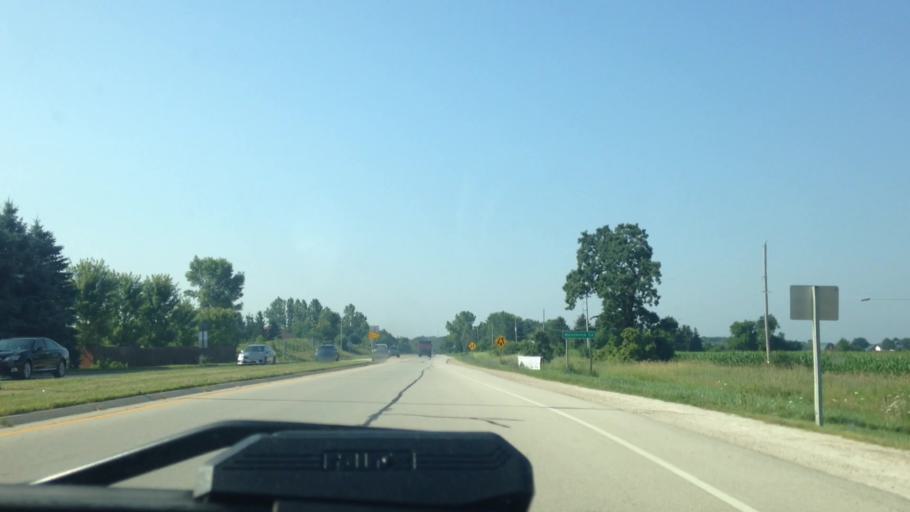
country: US
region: Wisconsin
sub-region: Waukesha County
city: Merton
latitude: 43.1924
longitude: -88.2615
